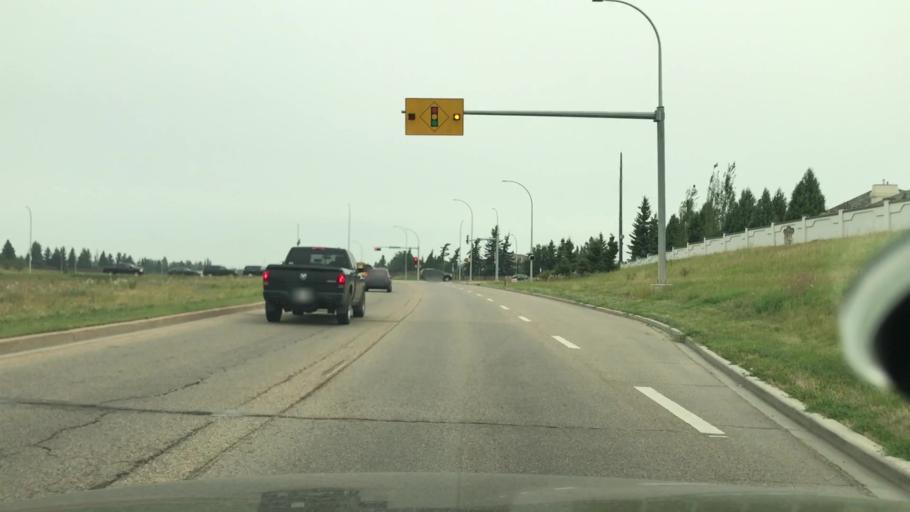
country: CA
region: Alberta
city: Edmonton
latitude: 53.4672
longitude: -113.5818
